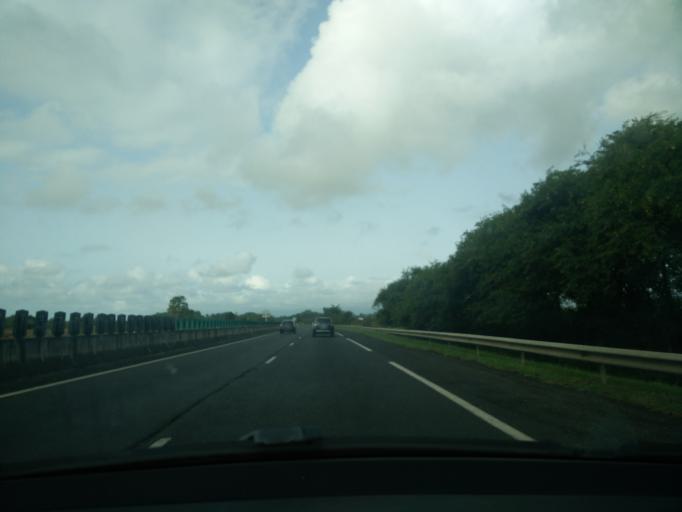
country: GP
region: Guadeloupe
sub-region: Guadeloupe
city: Les Abymes
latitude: 16.2973
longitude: -61.4994
